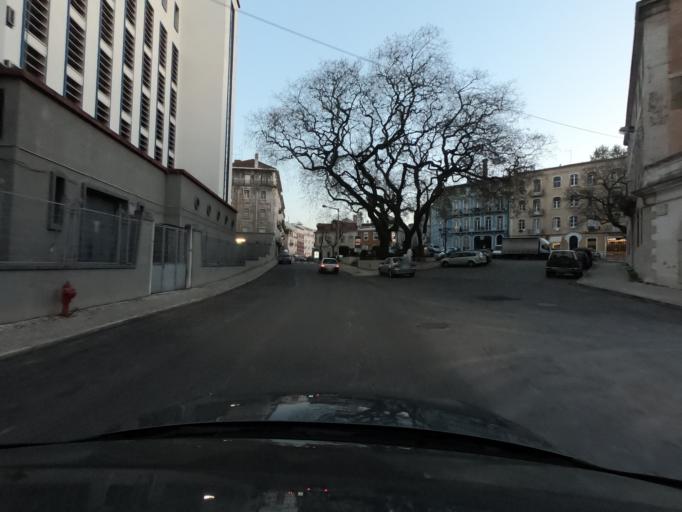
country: PT
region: Lisbon
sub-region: Lisbon
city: Lisbon
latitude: 38.7342
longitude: -9.1053
